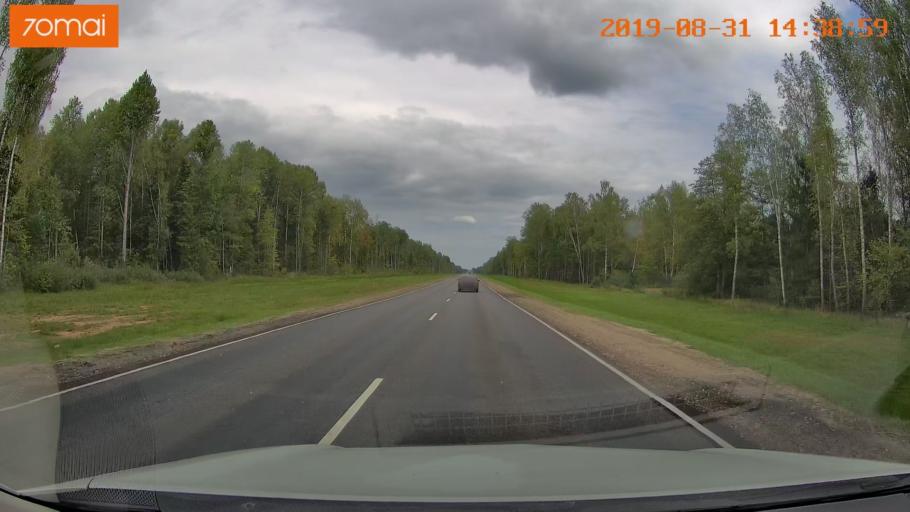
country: RU
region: Smolensk
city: Yekimovichi
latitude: 54.1884
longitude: 33.5416
